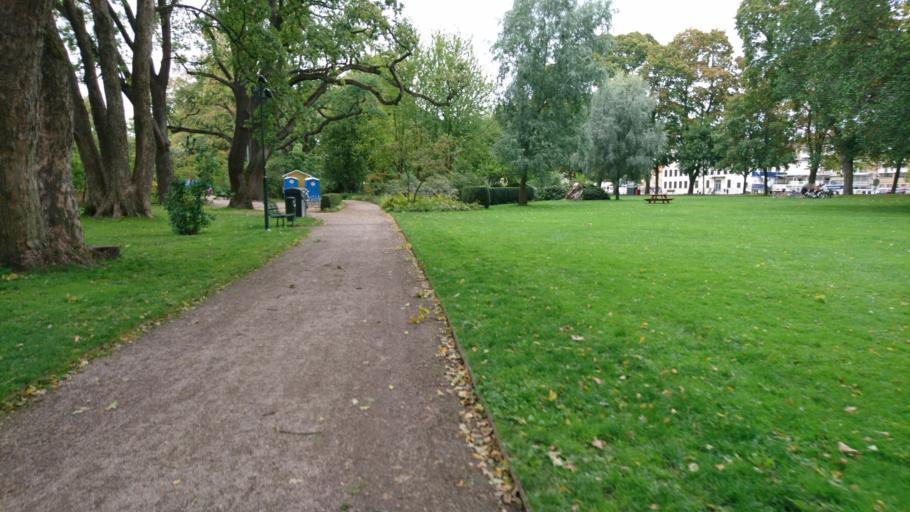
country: SE
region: Uppsala
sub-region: Uppsala Kommun
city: Uppsala
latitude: 59.8522
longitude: 17.6431
